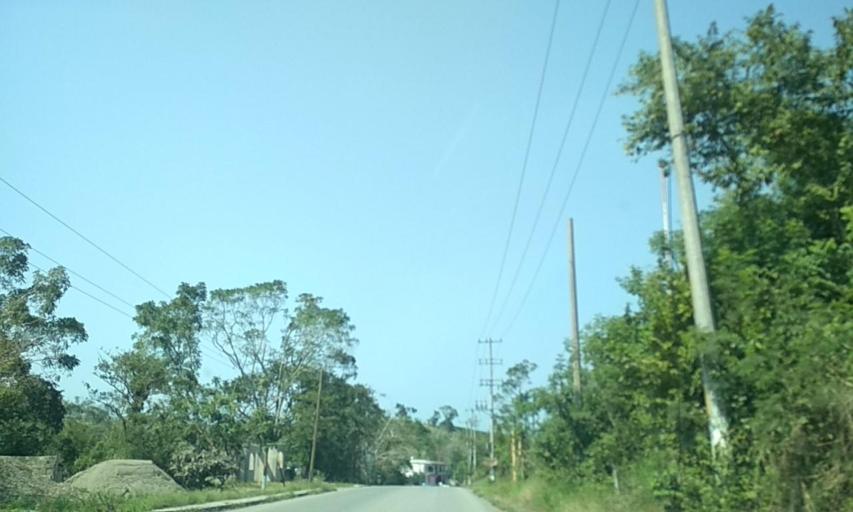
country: MX
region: Veracruz
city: Agua Dulce
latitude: 20.3727
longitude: -97.1812
